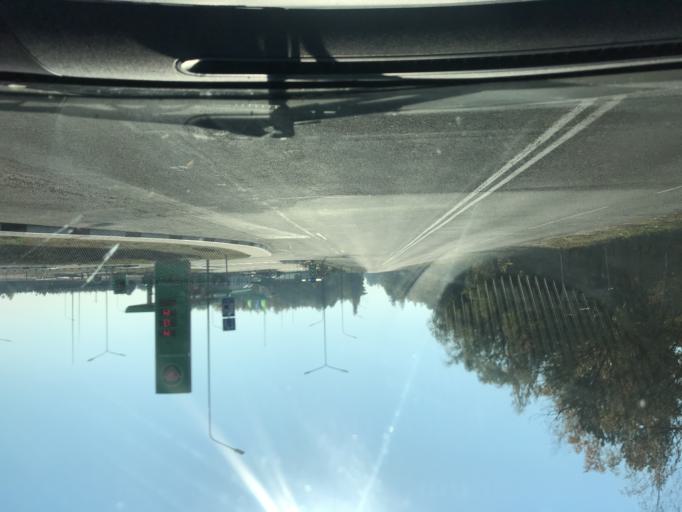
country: BY
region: Brest
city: Davyd-Haradok
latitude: 52.2473
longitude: 27.0839
